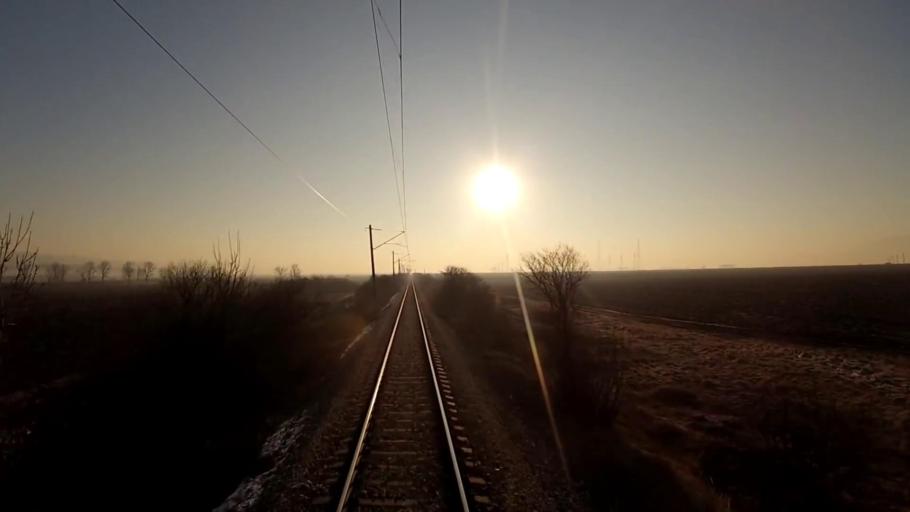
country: BG
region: Sofiya
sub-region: Obshtina Kostinbrod
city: Kostinbrod
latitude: 42.8156
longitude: 23.1842
